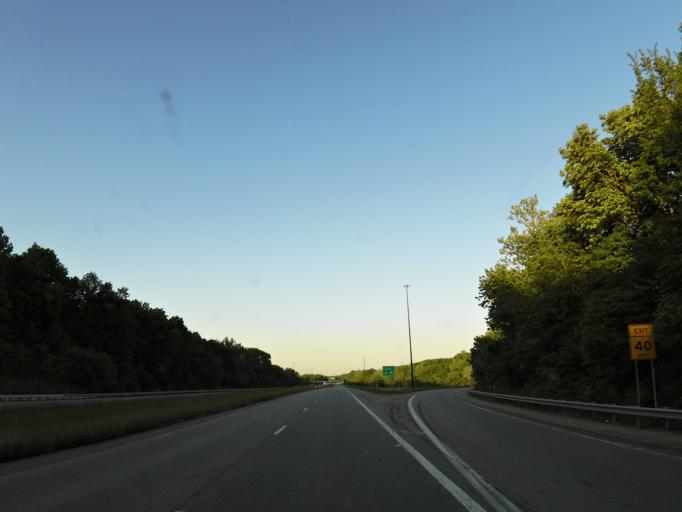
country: US
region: Indiana
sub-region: Fountain County
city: Covington
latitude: 40.1193
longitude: -87.4616
